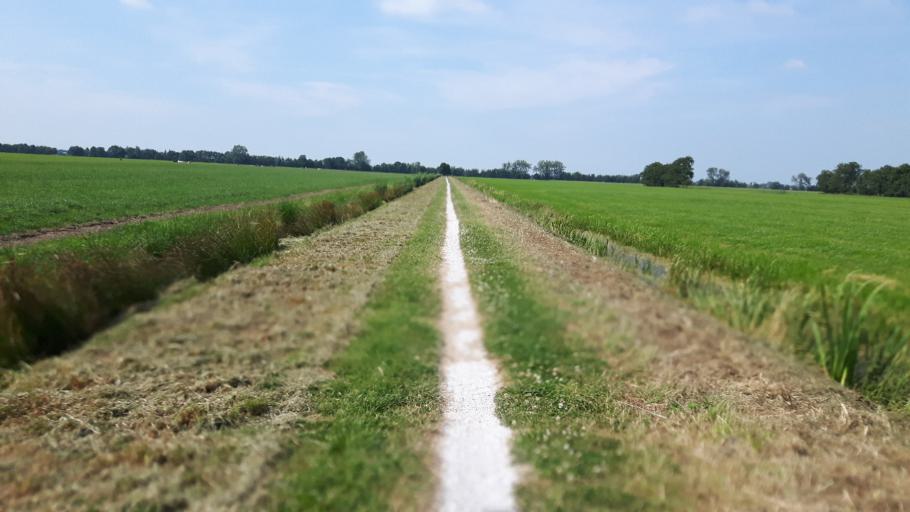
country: NL
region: South Holland
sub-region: Gemeente Schoonhoven
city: Schoonhoven
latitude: 51.9711
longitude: 4.8956
